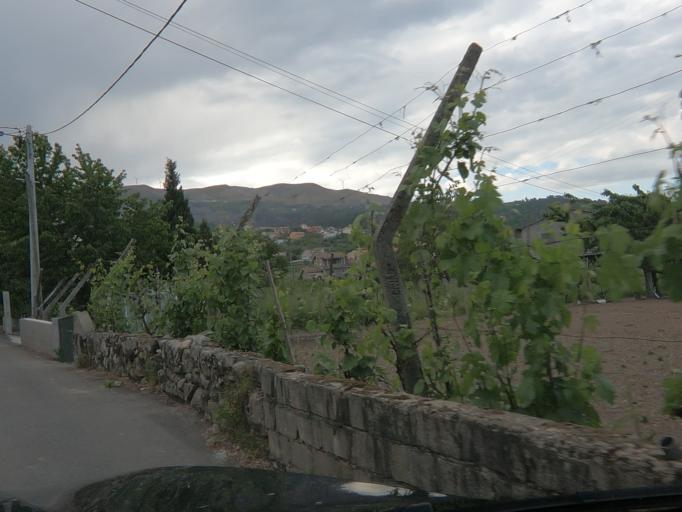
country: PT
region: Vila Real
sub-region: Vila Real
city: Vila Real
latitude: 41.3224
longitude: -7.7468
